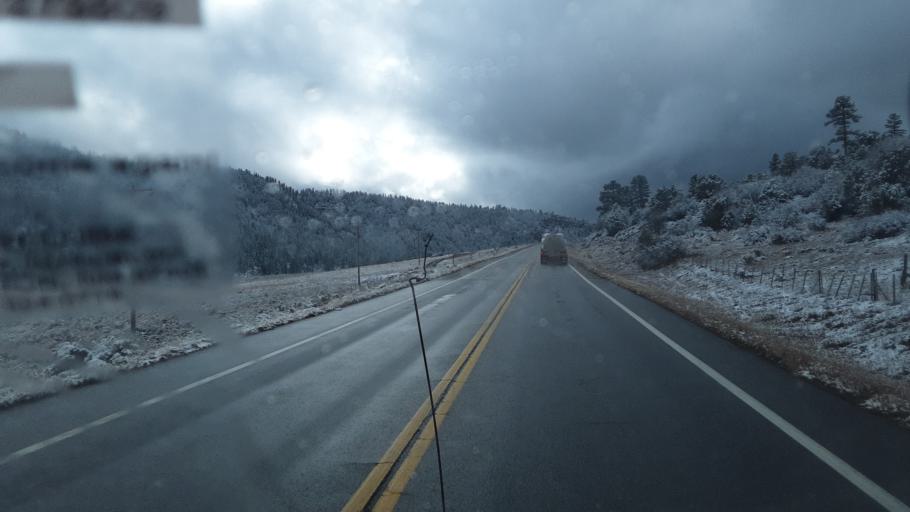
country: US
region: Colorado
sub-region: Archuleta County
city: Pagosa Springs
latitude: 37.2217
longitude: -107.2189
